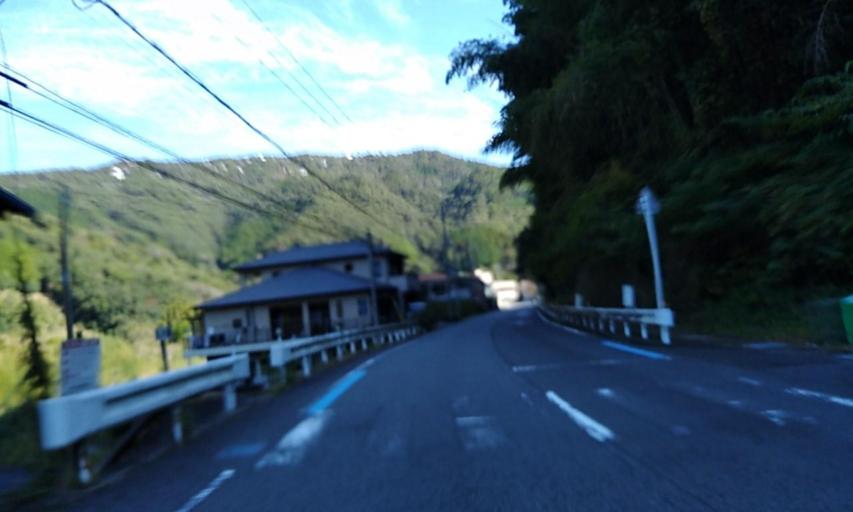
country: JP
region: Wakayama
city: Kainan
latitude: 34.0511
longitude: 135.3378
